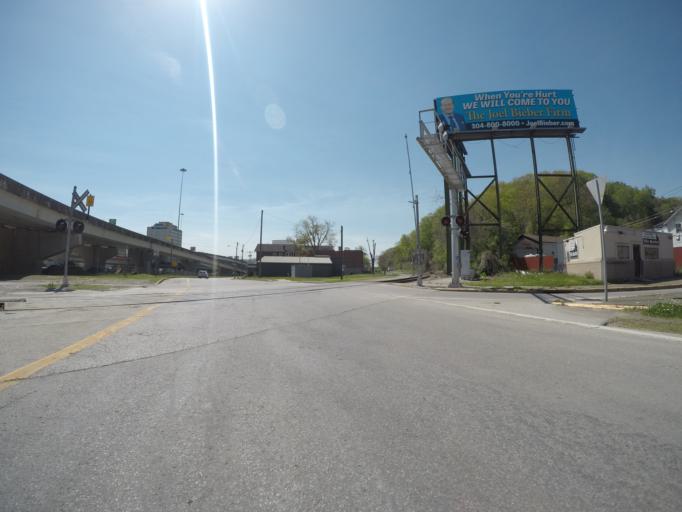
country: US
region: West Virginia
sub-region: Kanawha County
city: Charleston
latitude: 38.3608
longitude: -81.6313
